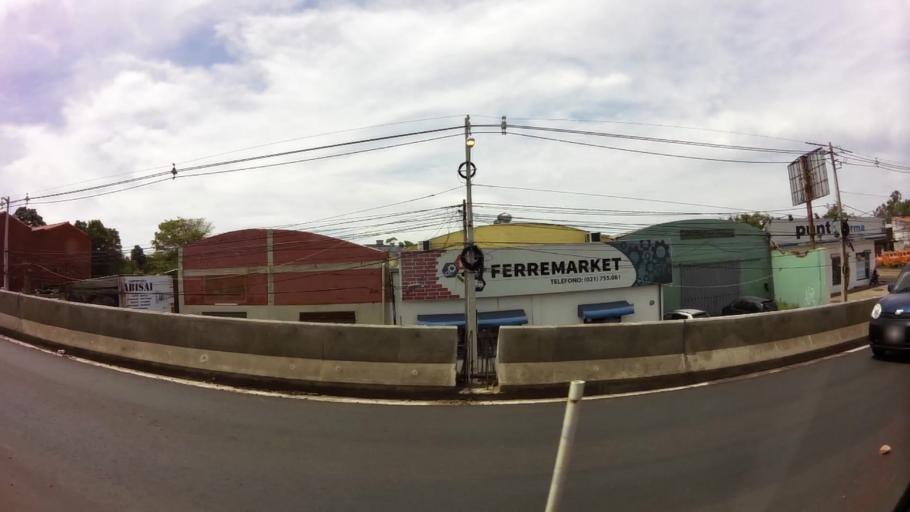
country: PY
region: Central
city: Colonia Mariano Roque Alonso
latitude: -25.2042
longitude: -57.5250
